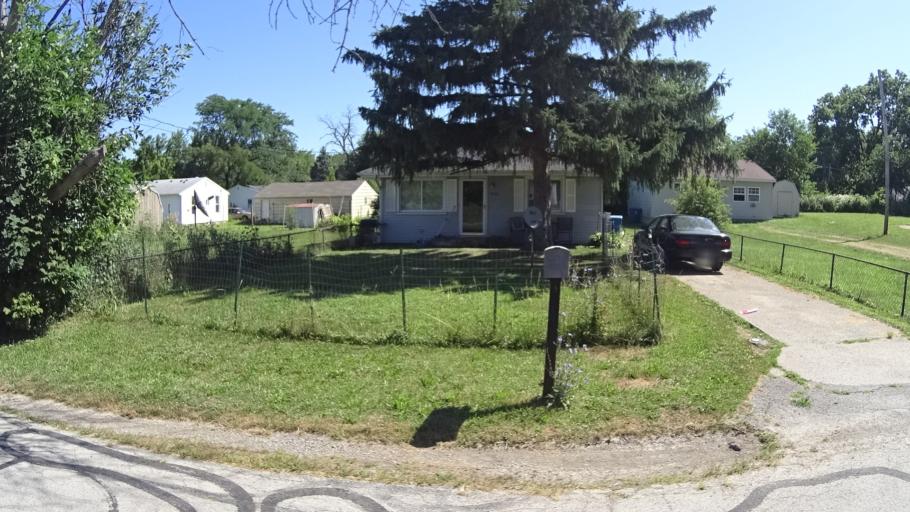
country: US
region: Ohio
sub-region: Erie County
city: Sandusky
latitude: 41.4220
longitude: -82.6863
